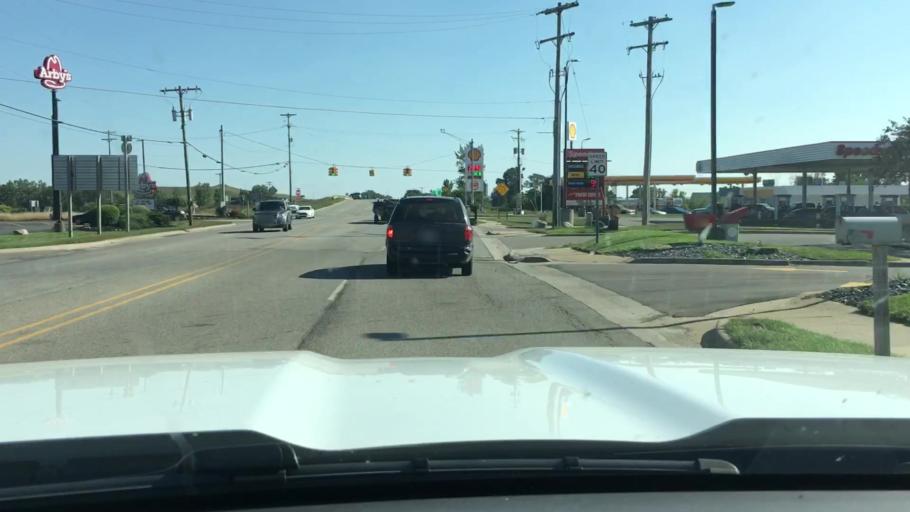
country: US
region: Michigan
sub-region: Ottawa County
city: Coopersville
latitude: 43.0587
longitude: -85.9569
